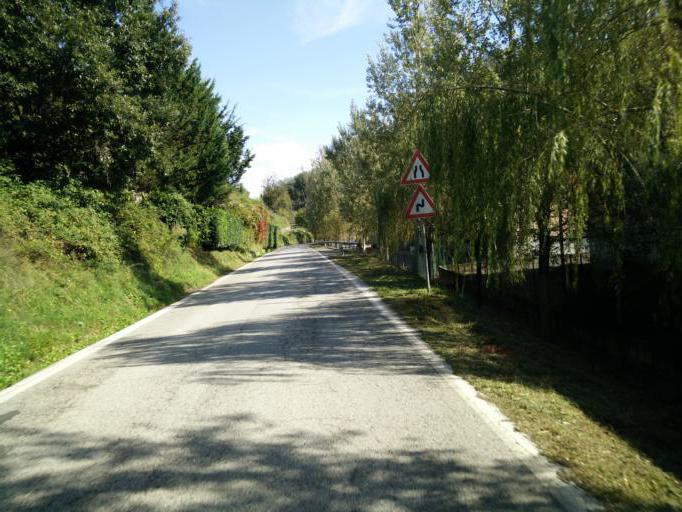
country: IT
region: Liguria
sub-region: Provincia di La Spezia
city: Carrodano
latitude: 44.2409
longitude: 9.6628
